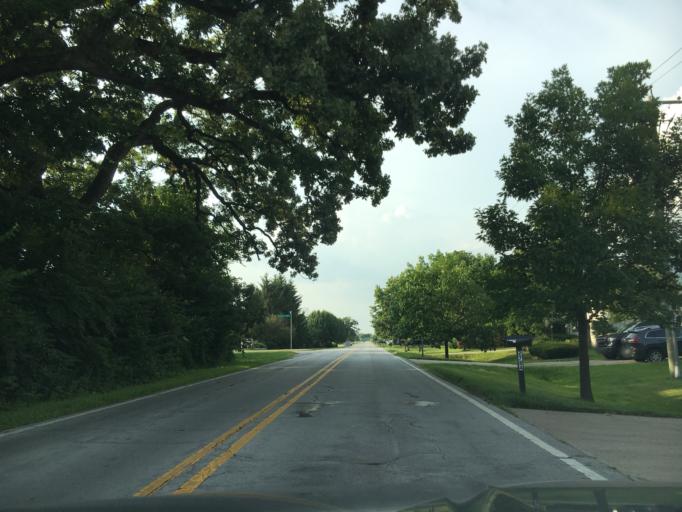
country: US
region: Ohio
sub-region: Franklin County
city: Hilliard
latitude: 40.0079
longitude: -83.1665
